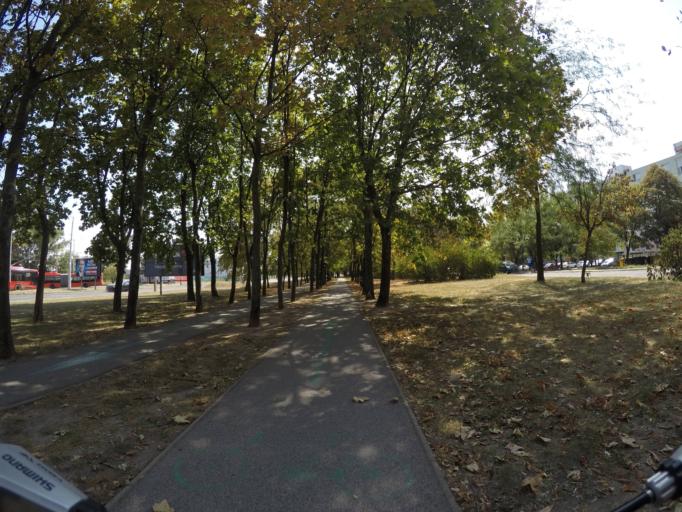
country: SK
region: Bratislavsky
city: Dunajska Luzna
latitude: 48.1444
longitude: 17.2121
